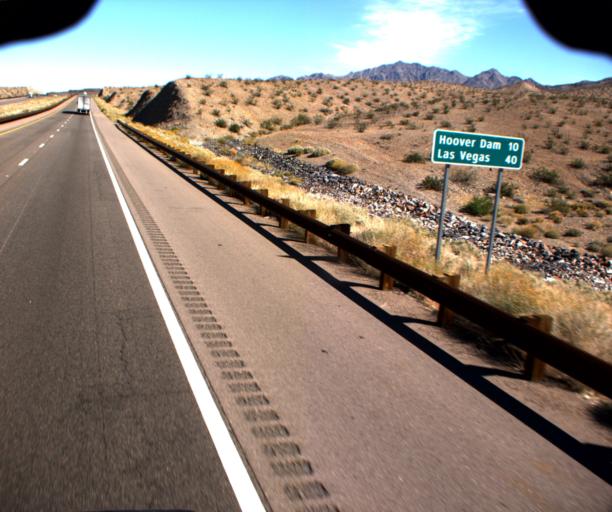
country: US
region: Nevada
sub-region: Clark County
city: Boulder City
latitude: 35.9202
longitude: -114.6310
